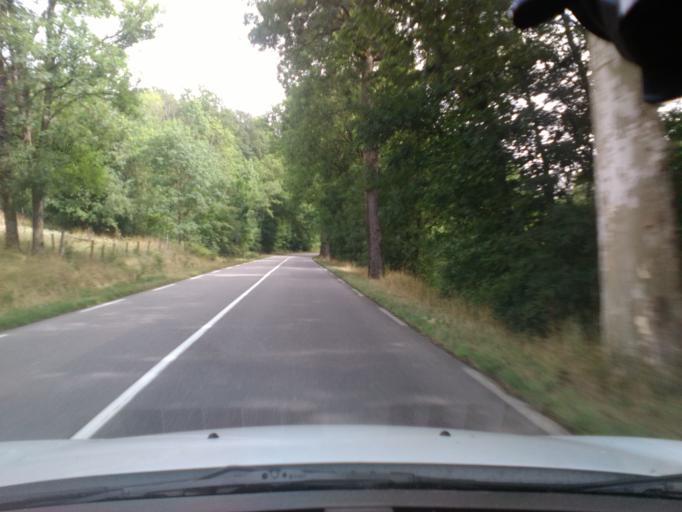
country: FR
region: Lorraine
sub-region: Departement de Meurthe-et-Moselle
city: Pulligny
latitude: 48.5257
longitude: 6.1698
